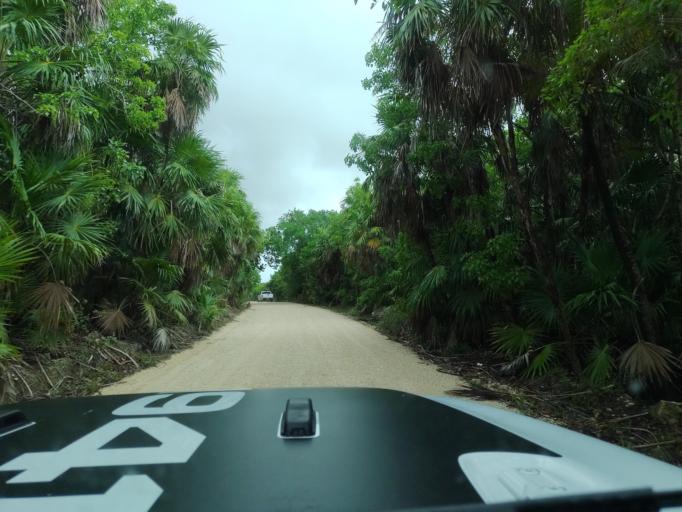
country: MX
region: Quintana Roo
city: Tulum
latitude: 20.0669
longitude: -87.4791
